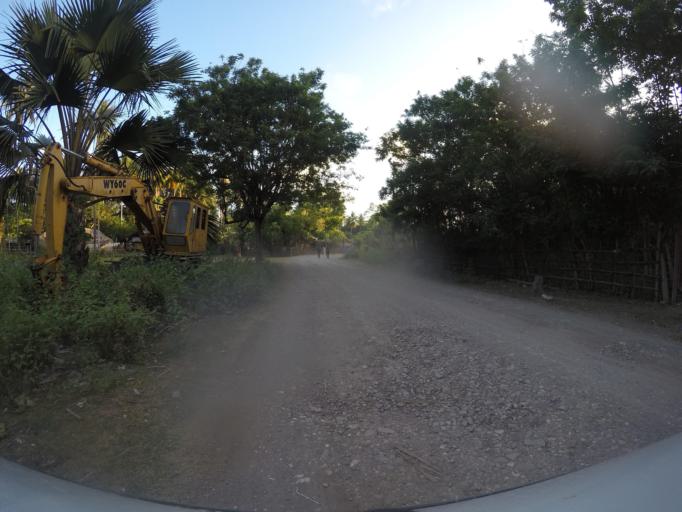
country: TL
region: Baucau
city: Venilale
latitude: -8.7456
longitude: 126.7133
